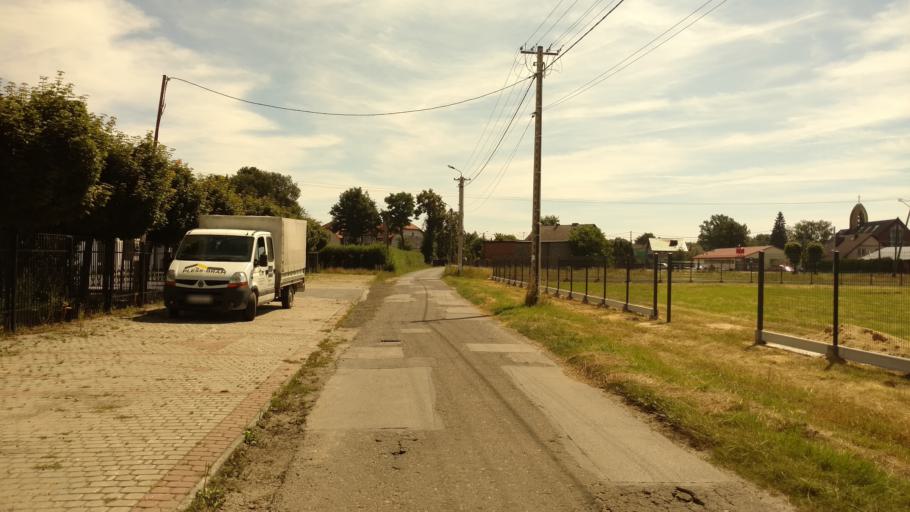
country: PL
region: Silesian Voivodeship
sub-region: Powiat pszczynski
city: Jankowice
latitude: 50.0026
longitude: 18.9843
